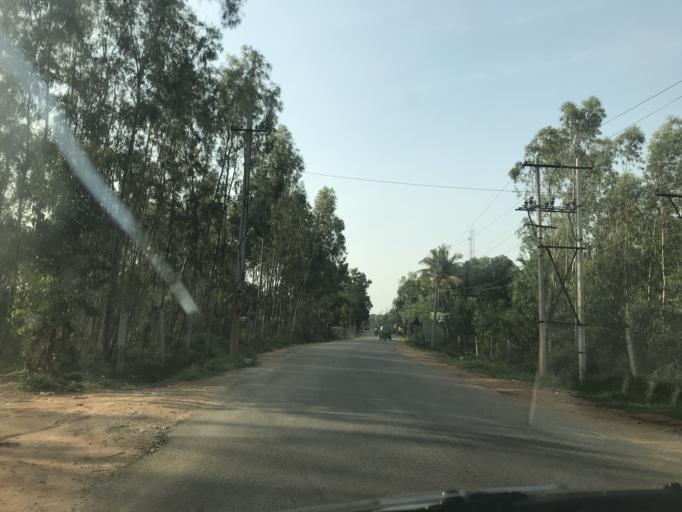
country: IN
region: Karnataka
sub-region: Bangalore Rural
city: Devanhalli
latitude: 13.1945
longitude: 77.6455
